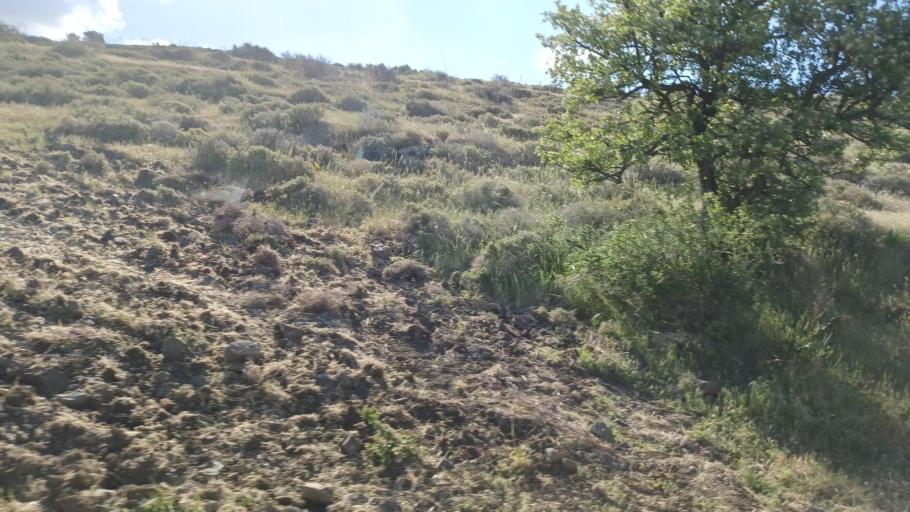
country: CY
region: Lefkosia
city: Peristerona
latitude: 35.0661
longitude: 33.0527
